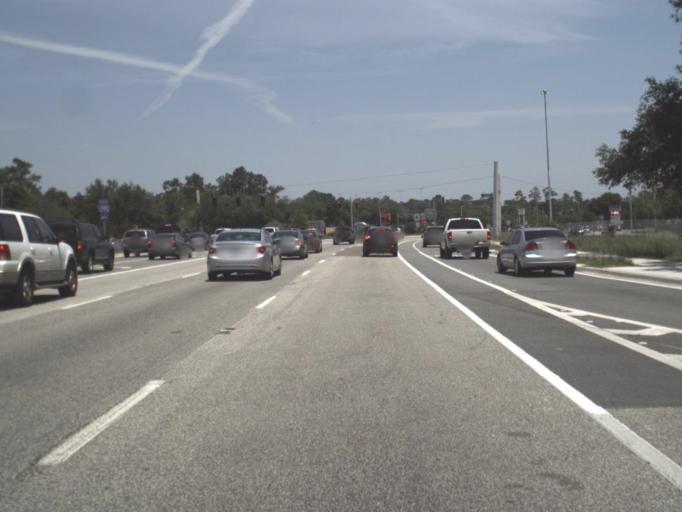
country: US
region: Florida
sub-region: Saint Johns County
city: Fruit Cove
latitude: 30.1823
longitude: -81.6284
